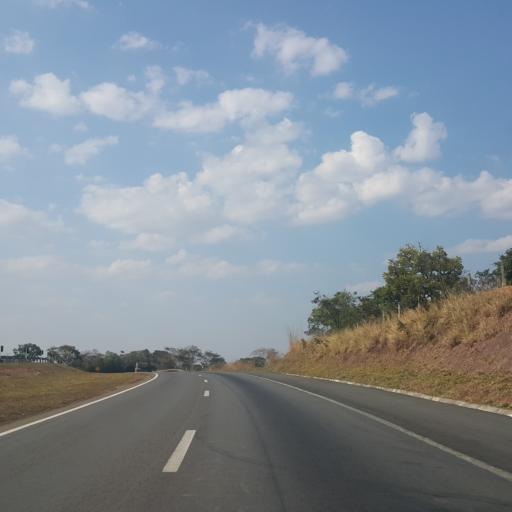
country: BR
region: Goias
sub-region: Abadiania
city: Abadiania
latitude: -16.1664
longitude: -48.6345
